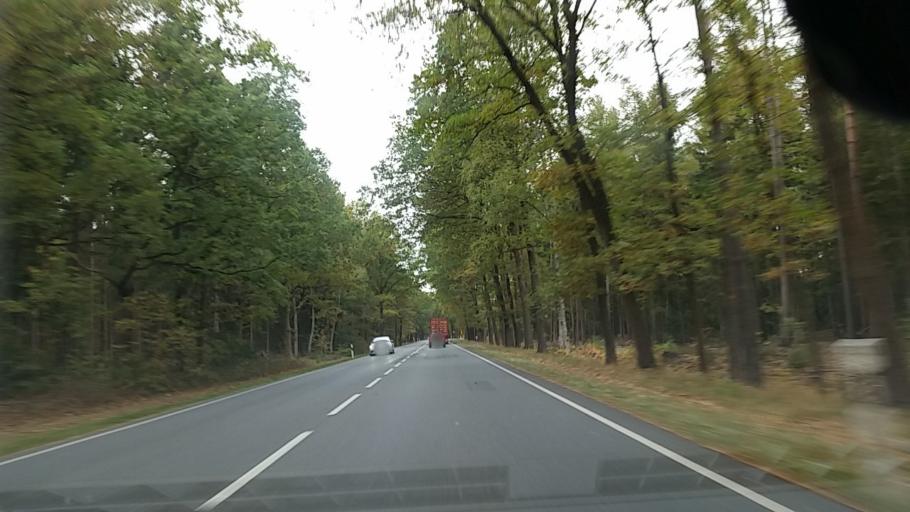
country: DE
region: Lower Saxony
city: Sprakensehl
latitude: 52.7841
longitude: 10.4912
